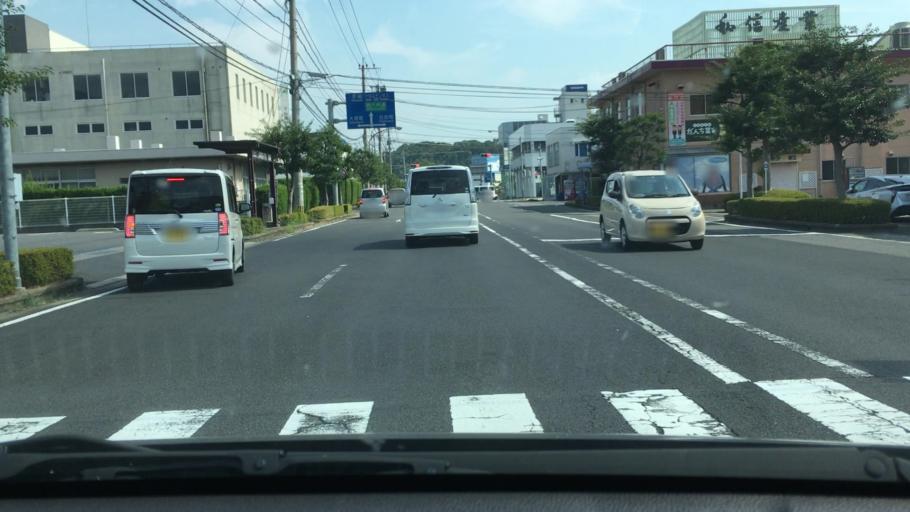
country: JP
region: Nagasaki
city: Sasebo
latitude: 33.1512
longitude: 129.7709
